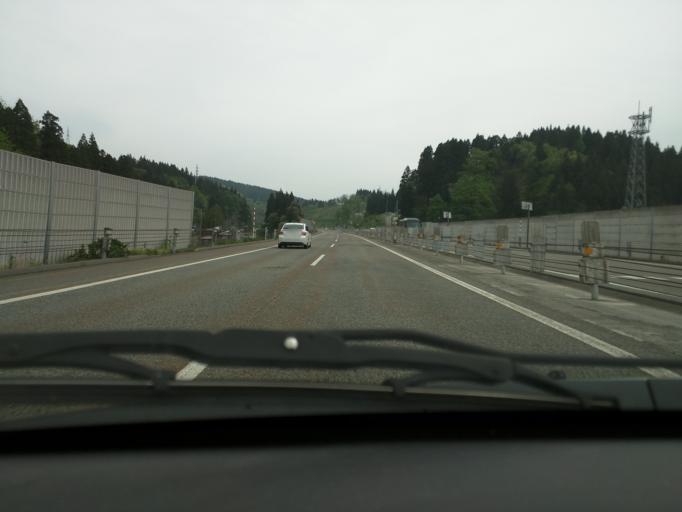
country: JP
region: Niigata
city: Ojiya
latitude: 37.2847
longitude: 138.7860
